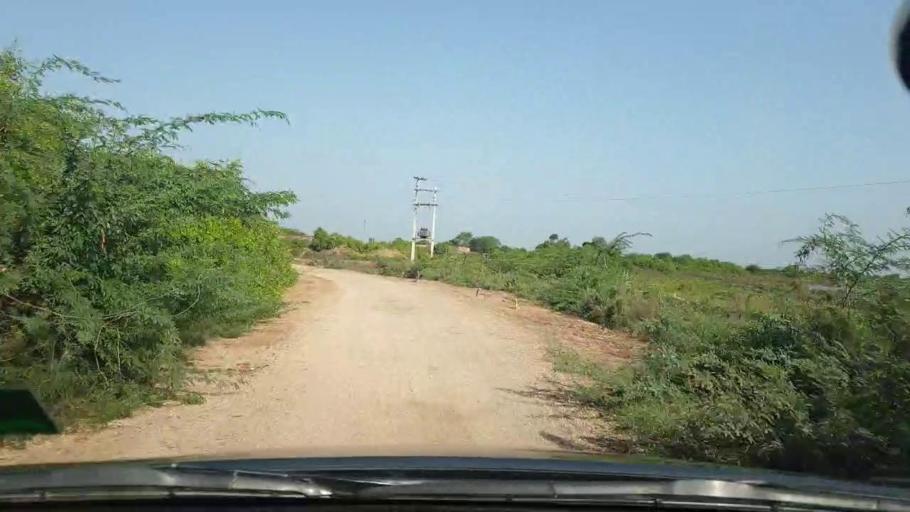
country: PK
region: Sindh
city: Tando Bago
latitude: 24.6867
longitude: 69.0094
